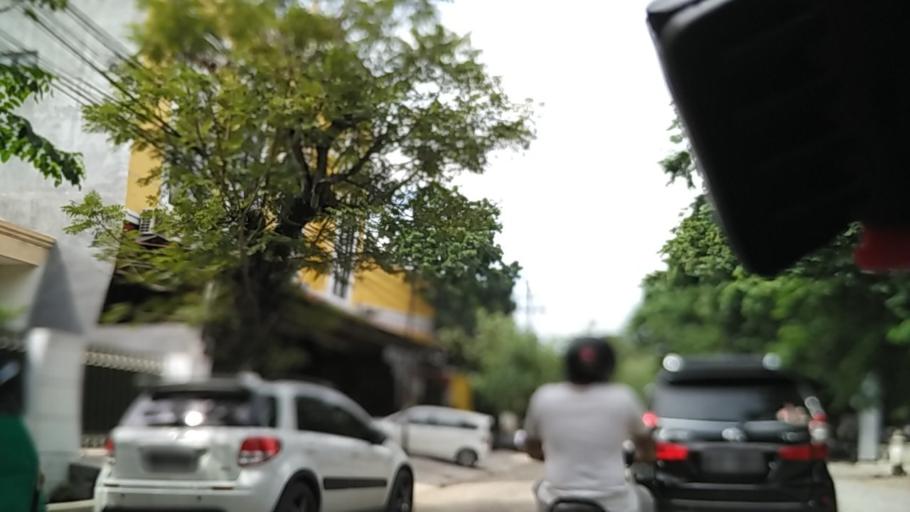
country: ID
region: Central Java
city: Semarang
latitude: -6.9977
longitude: 110.4280
